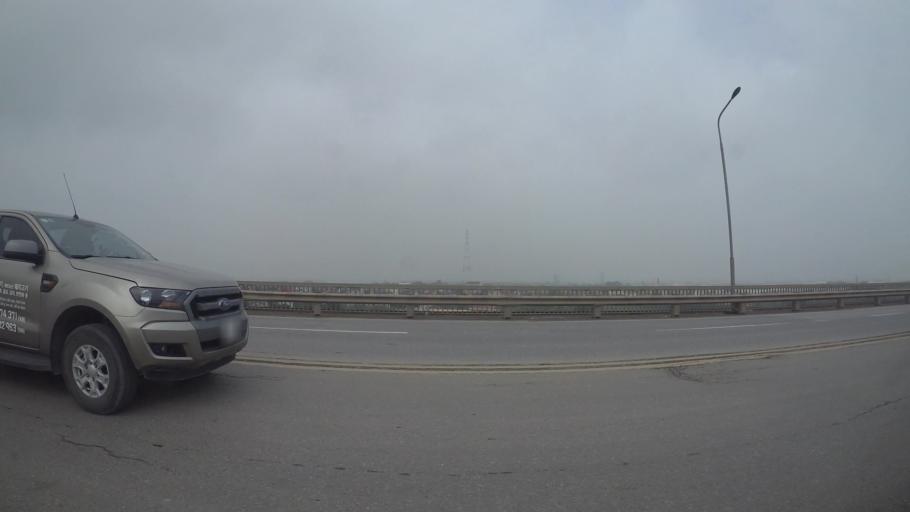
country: VN
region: Ha Noi
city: Tay Ho
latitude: 21.1040
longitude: 105.7869
